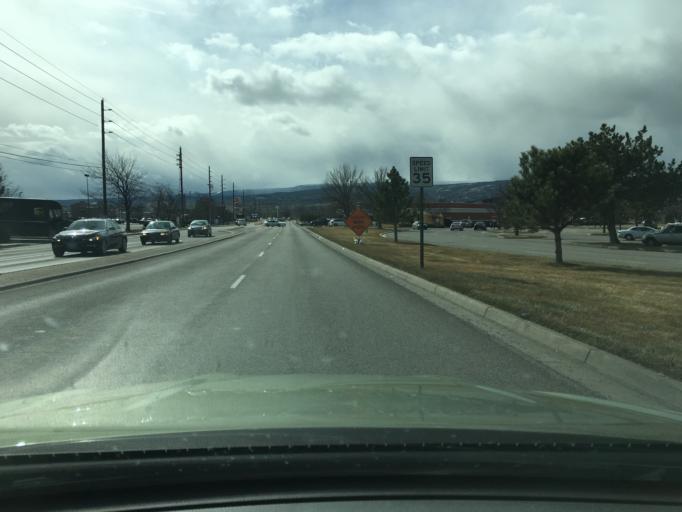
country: US
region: Colorado
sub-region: Mesa County
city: Redlands
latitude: 39.0916
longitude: -108.5989
